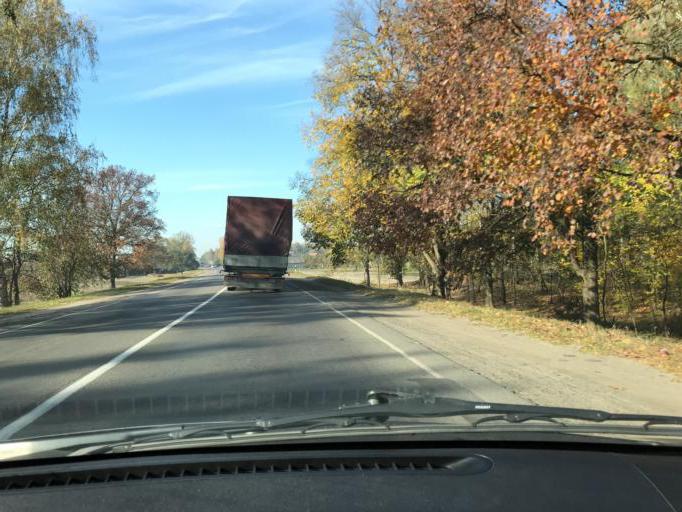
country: BY
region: Brest
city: Luninyets
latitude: 52.2773
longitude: 26.9525
